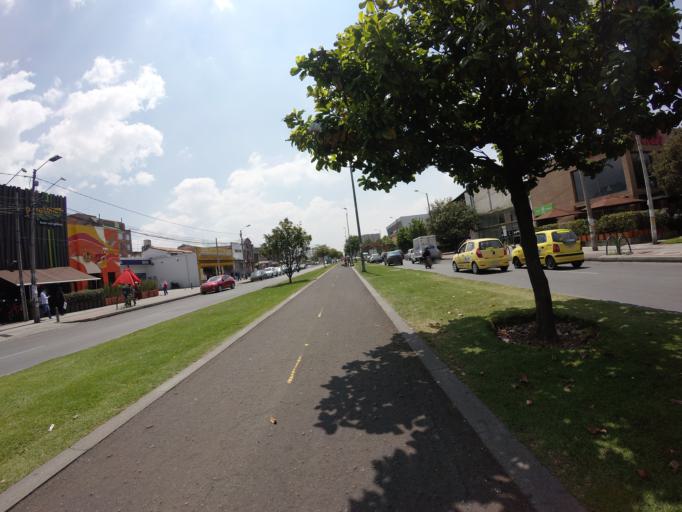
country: CO
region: Bogota D.C.
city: Barrio San Luis
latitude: 4.7228
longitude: -74.0464
